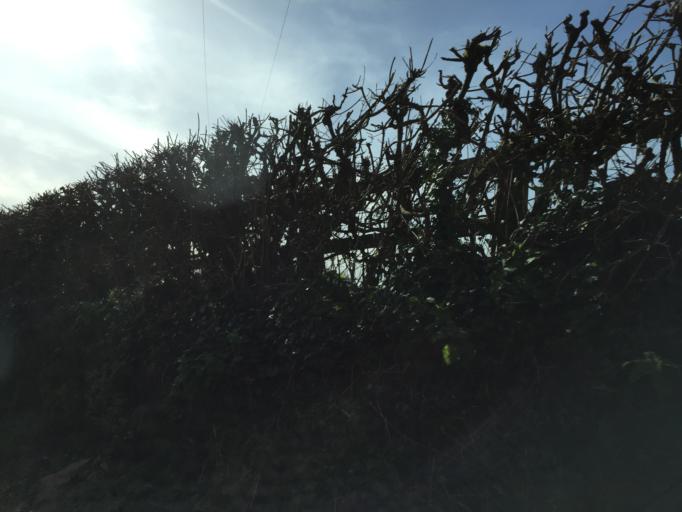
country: GB
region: England
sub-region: Wiltshire
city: Chippenham
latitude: 51.5001
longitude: -2.1518
